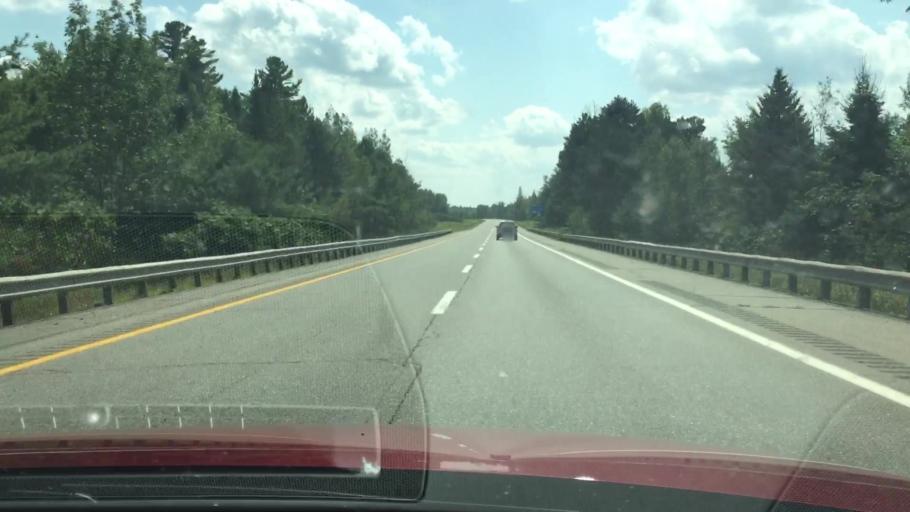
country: US
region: Maine
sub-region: Penobscot County
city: Lincoln
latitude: 45.3915
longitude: -68.6030
